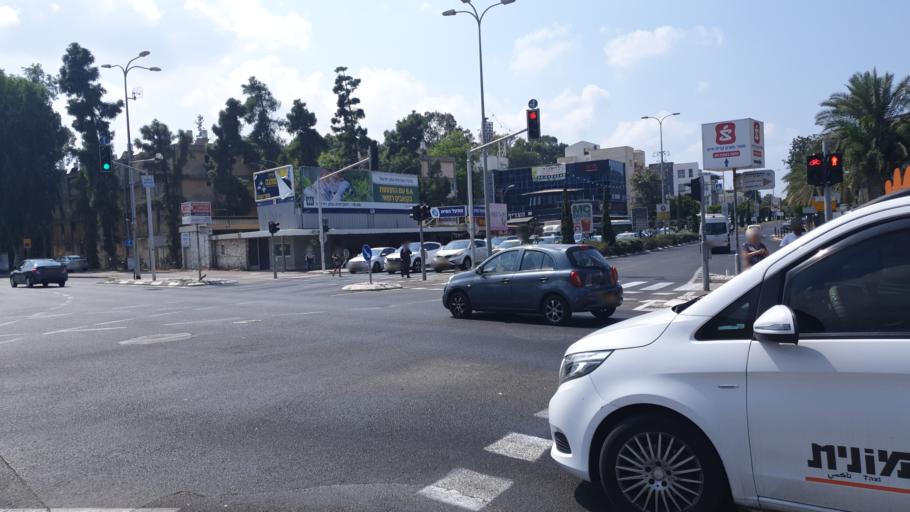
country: IL
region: Haifa
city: Qiryat Bialik
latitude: 32.8177
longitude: 35.0775
